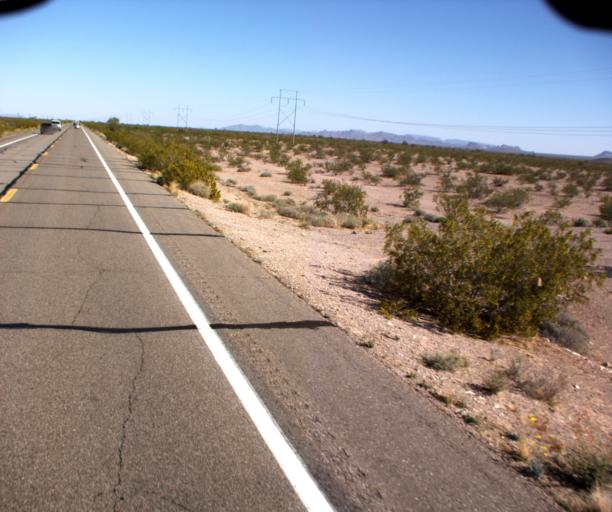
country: US
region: Arizona
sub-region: La Paz County
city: Quartzsite
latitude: 33.3256
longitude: -114.2169
